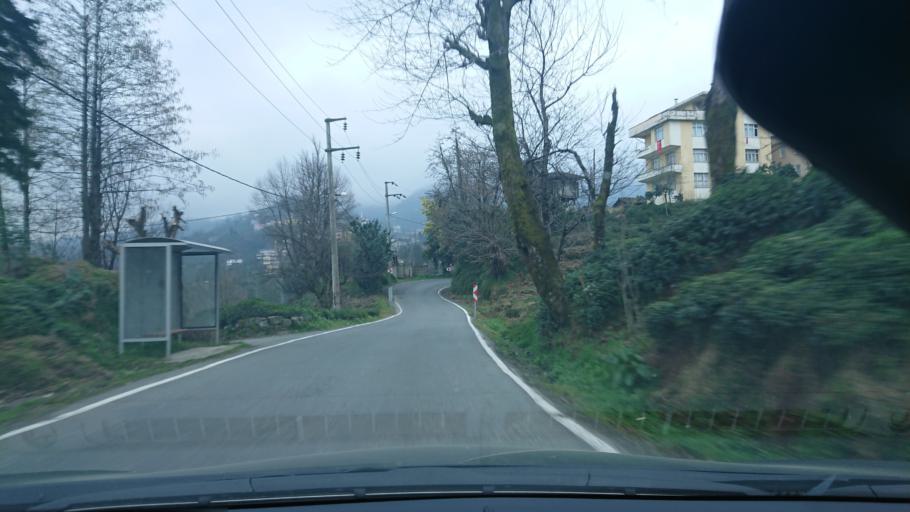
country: TR
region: Rize
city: Rize
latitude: 41.0017
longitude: 40.4871
